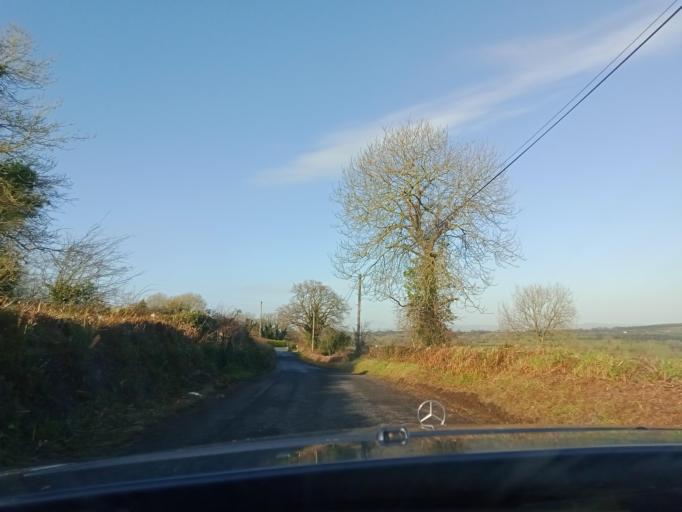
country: IE
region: Leinster
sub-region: Kilkenny
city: Callan
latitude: 52.4643
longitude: -7.3999
